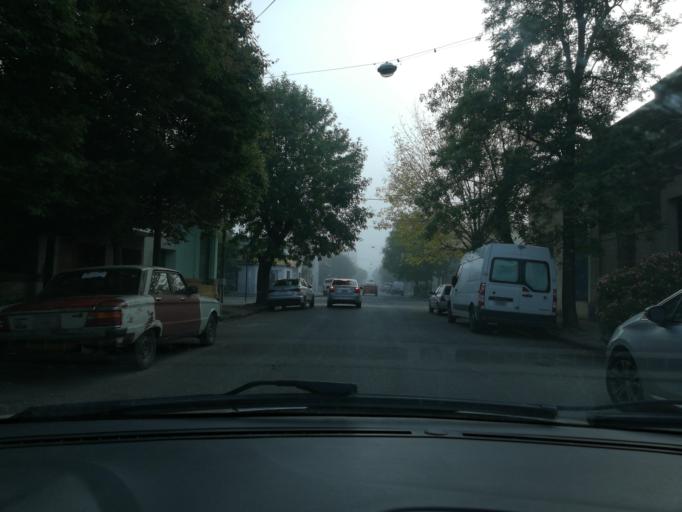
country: AR
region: Buenos Aires
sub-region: Partido de Balcarce
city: Balcarce
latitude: -37.8507
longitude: -58.2587
